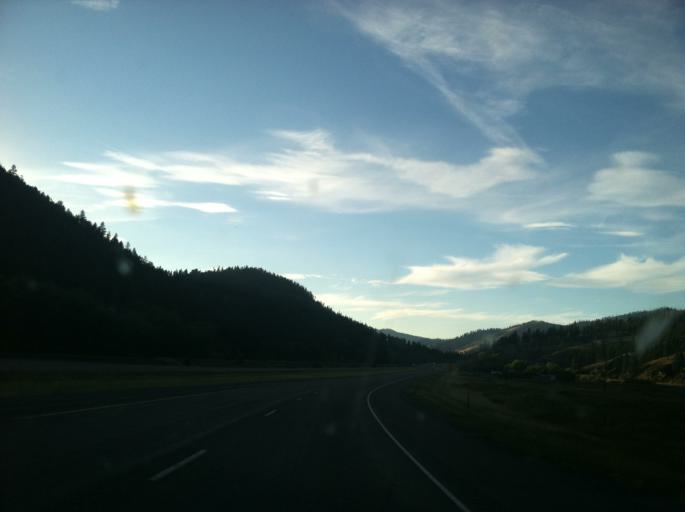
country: US
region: Montana
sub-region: Missoula County
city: Clinton
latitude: 46.6983
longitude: -113.4899
